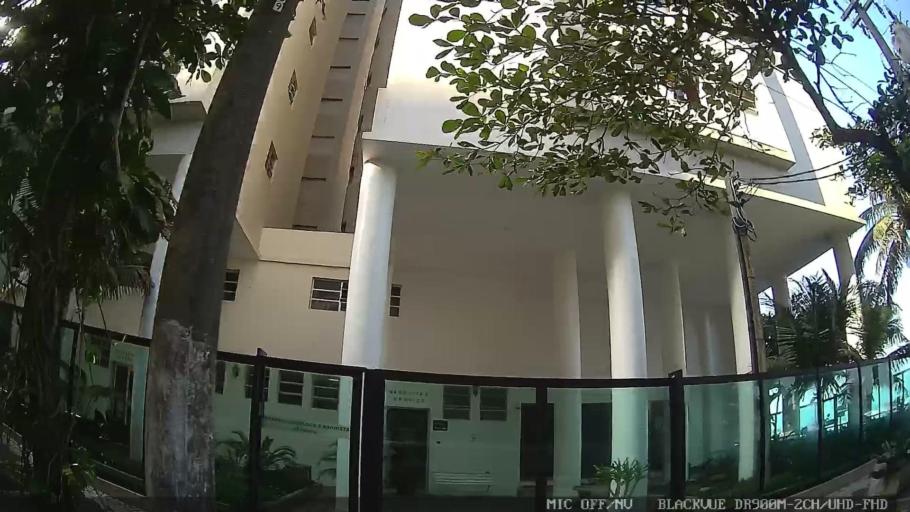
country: BR
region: Sao Paulo
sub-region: Guaruja
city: Guaruja
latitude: -24.0002
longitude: -46.2628
